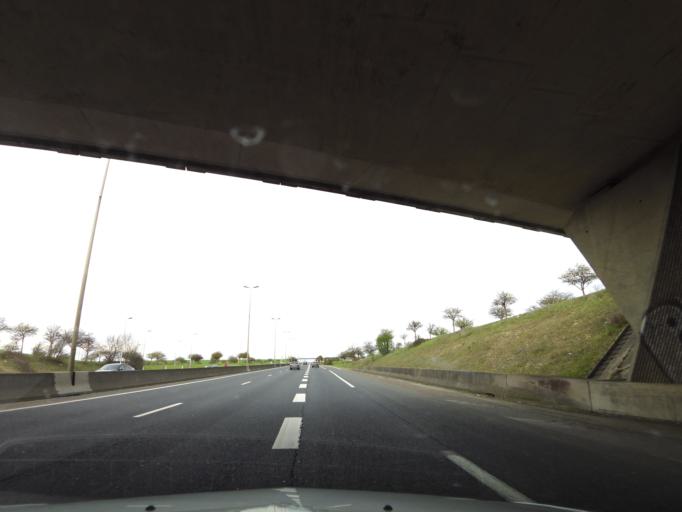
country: FR
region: Lower Normandy
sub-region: Departement du Calvados
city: Bretteville-sur-Odon
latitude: 49.1622
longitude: -0.4276
